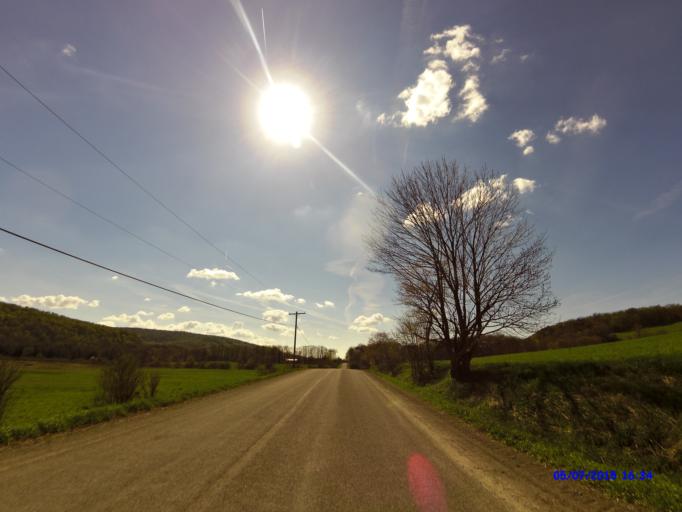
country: US
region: New York
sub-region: Cattaraugus County
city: Little Valley
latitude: 42.3270
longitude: -78.6759
